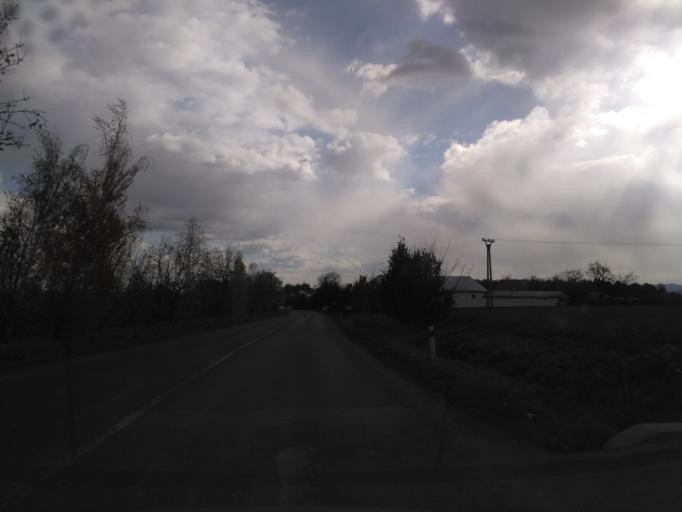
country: SK
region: Kosicky
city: Secovce
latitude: 48.6549
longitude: 21.6729
